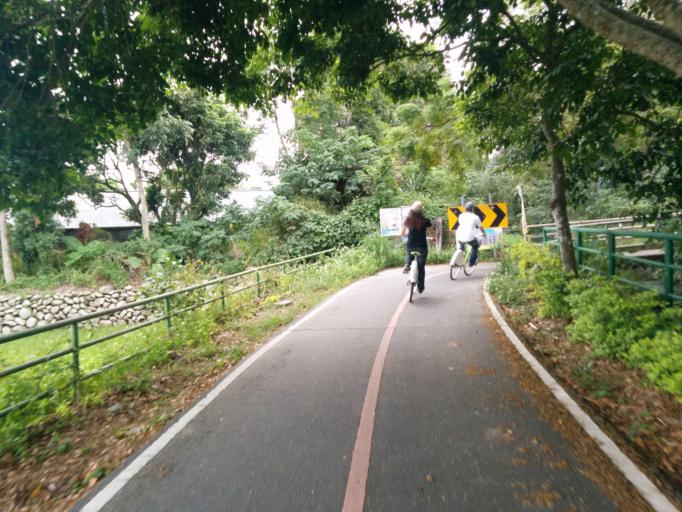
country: TW
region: Taiwan
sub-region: Taitung
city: Taitung
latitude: 23.0385
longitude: 121.1549
